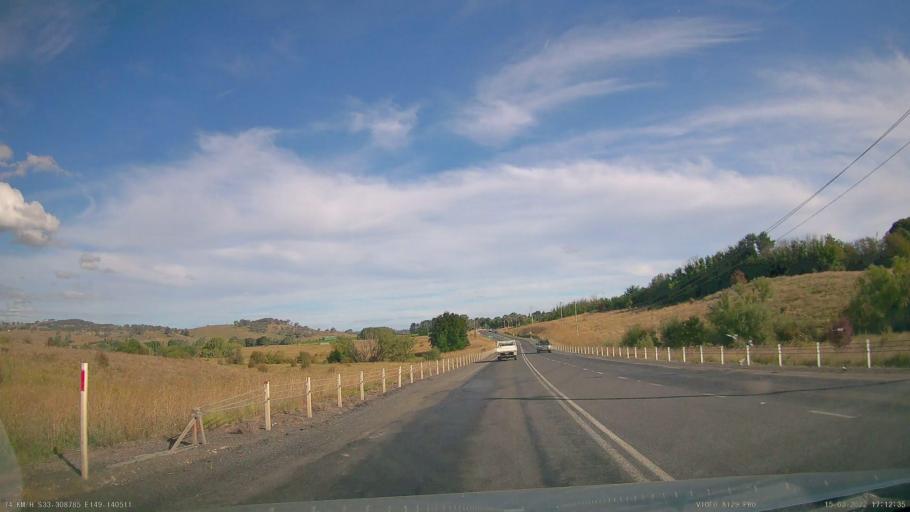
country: AU
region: New South Wales
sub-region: Orange Municipality
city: Orange
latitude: -33.3090
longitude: 149.1405
